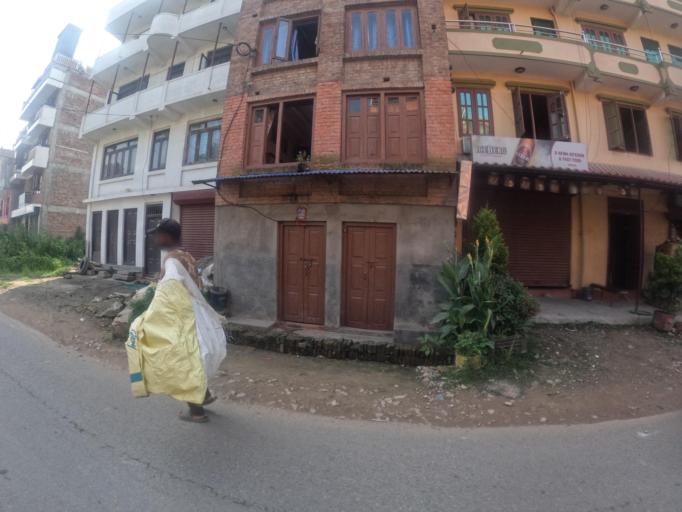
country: NP
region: Central Region
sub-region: Bagmati Zone
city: Bhaktapur
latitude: 27.6798
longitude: 85.4354
